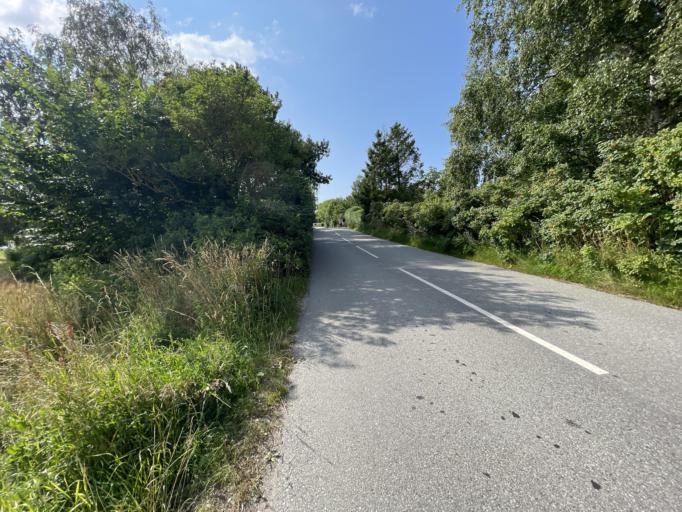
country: DK
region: Capital Region
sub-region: Gribskov Kommune
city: Helsinge
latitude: 56.0903
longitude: 12.1763
